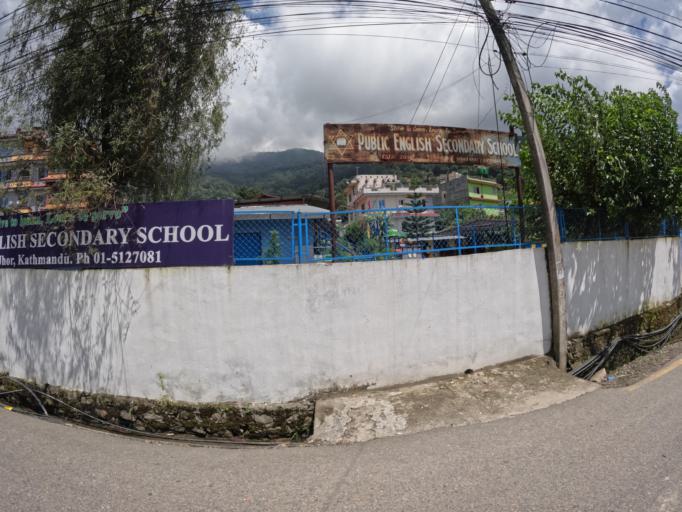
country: NP
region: Central Region
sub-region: Bagmati Zone
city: Kathmandu
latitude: 27.7929
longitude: 85.3301
